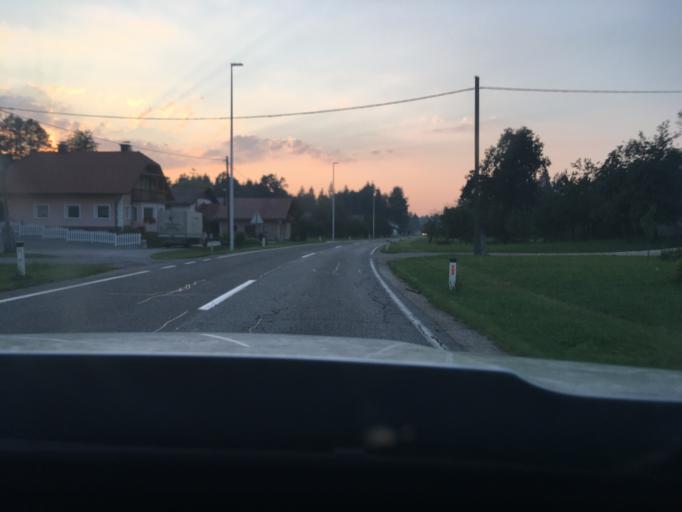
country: SI
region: Kocevje
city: Kocevje
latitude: 45.6742
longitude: 14.8291
